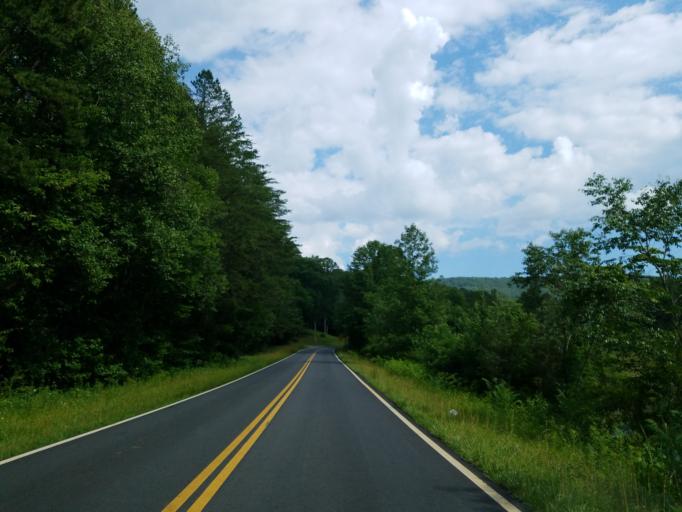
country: US
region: Georgia
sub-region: Fannin County
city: Blue Ridge
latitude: 34.8424
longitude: -84.2989
